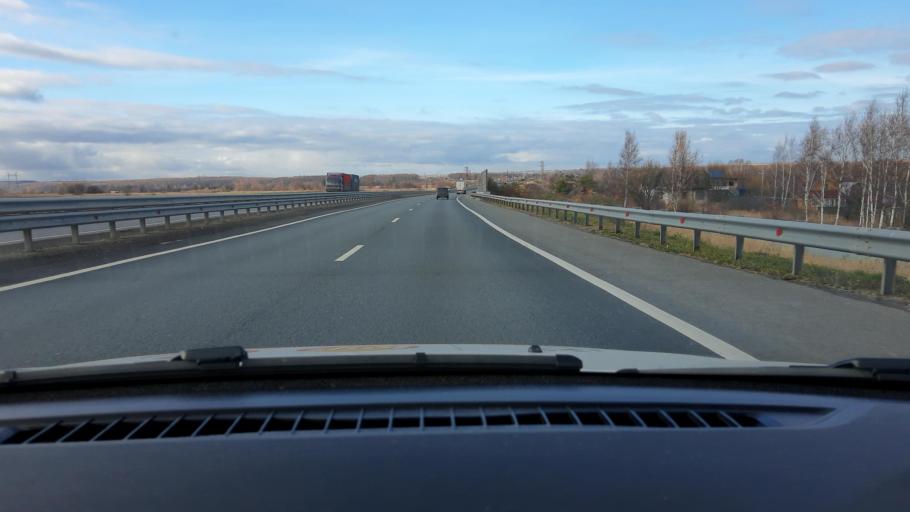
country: RU
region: Nizjnij Novgorod
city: Burevestnik
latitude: 56.1138
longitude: 43.8727
